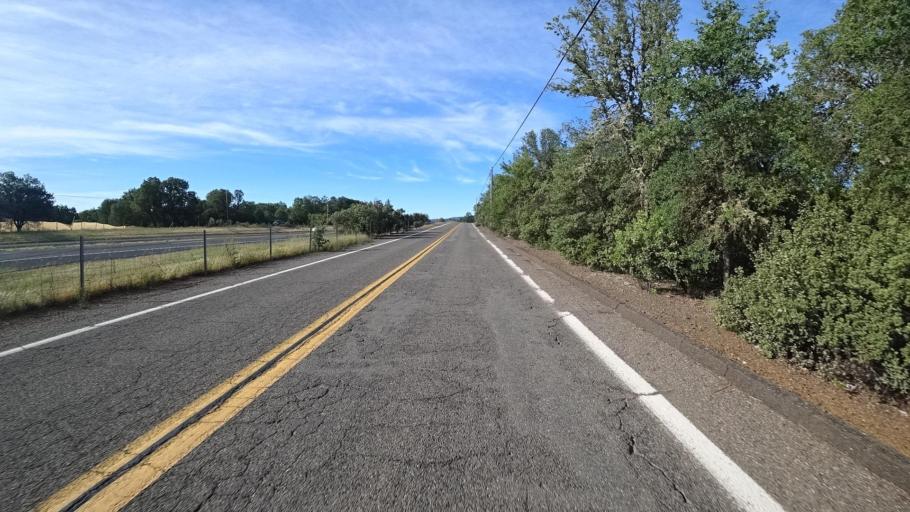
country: US
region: California
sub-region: Lake County
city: North Lakeport
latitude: 39.0708
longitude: -122.9316
